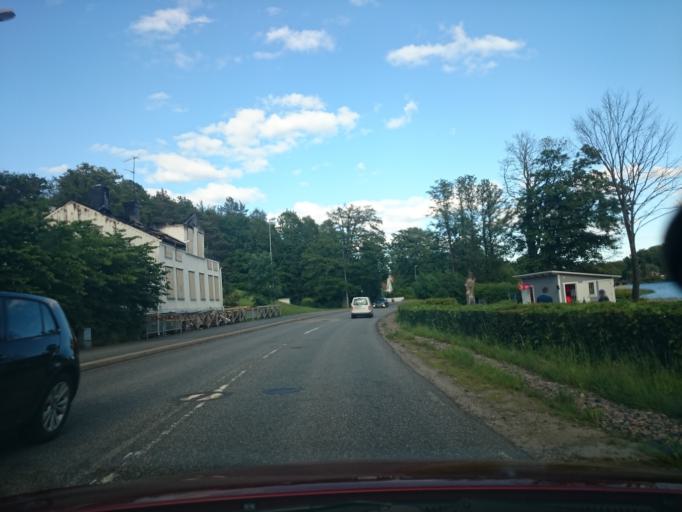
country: SE
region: Vaestra Goetaland
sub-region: Molndal
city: Moelndal
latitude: 57.6638
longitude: 12.0425
